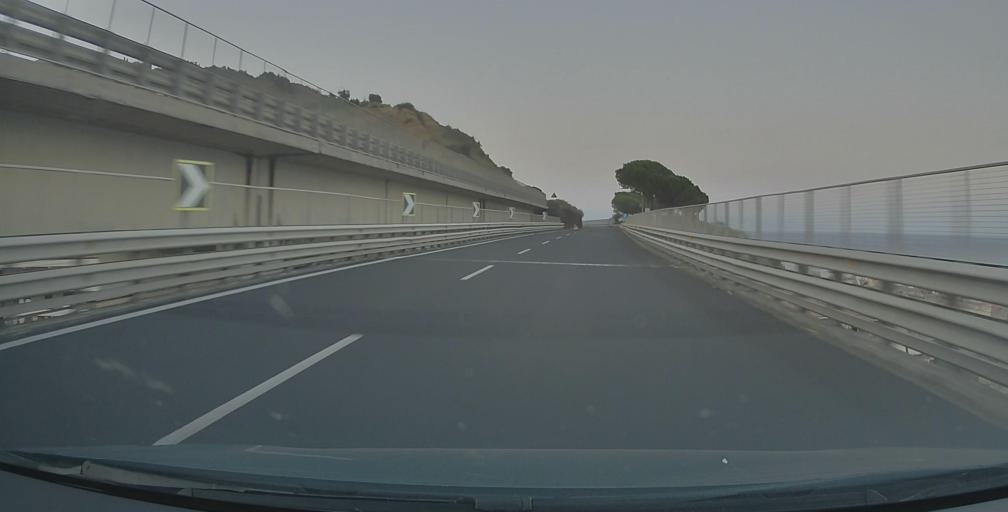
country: IT
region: Sicily
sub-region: Messina
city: Letojanni
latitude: 37.8816
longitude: 15.3051
